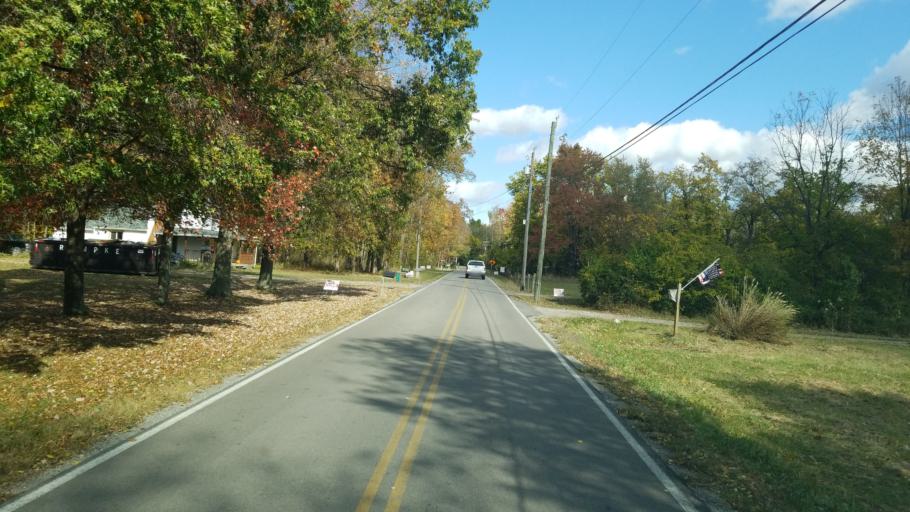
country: US
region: Ohio
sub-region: Warren County
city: Morrow
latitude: 39.3898
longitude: -84.1592
